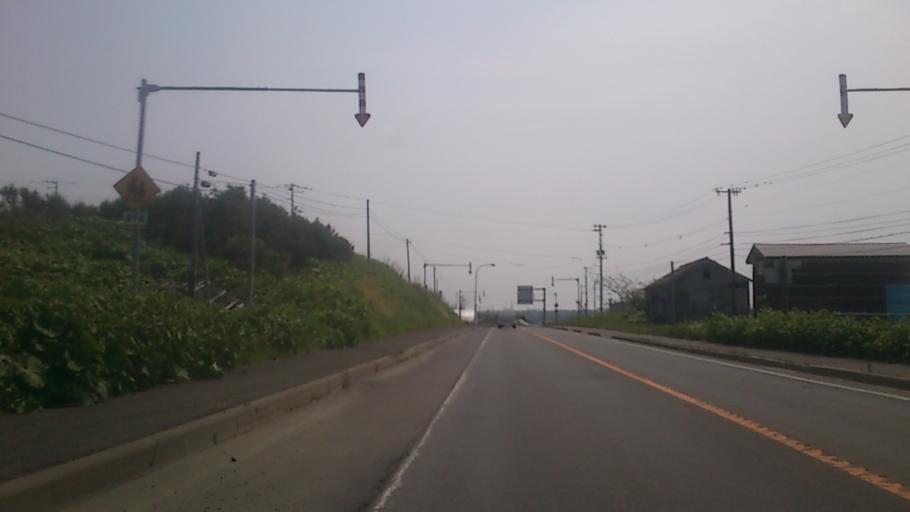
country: JP
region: Hokkaido
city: Nemuro
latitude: 43.2813
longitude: 145.5069
